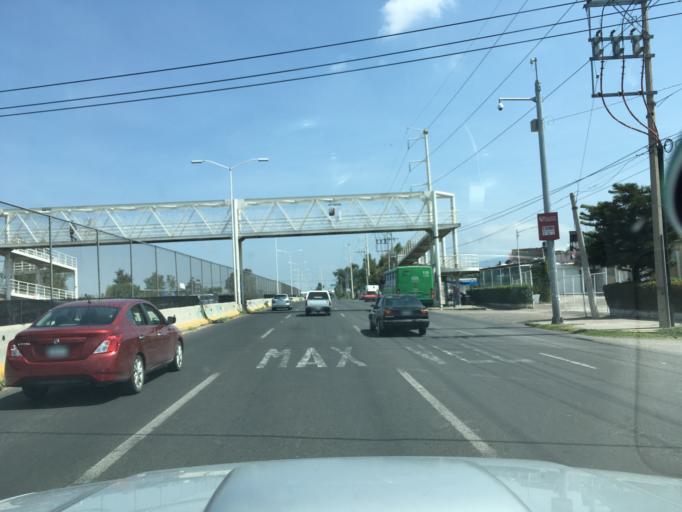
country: MX
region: Jalisco
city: Tonala
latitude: 20.6716
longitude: -103.2360
